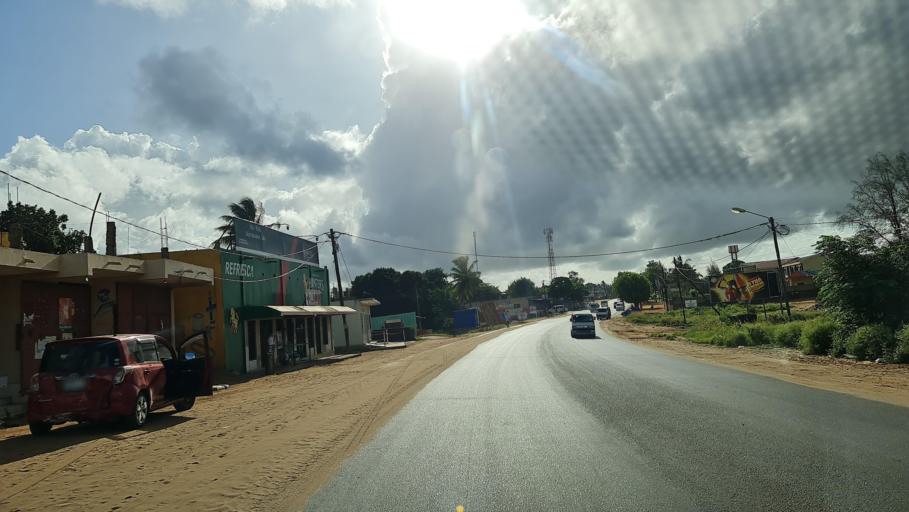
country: MZ
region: Gaza
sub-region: Xai-Xai District
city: Xai-Xai
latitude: -25.0555
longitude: 33.6680
